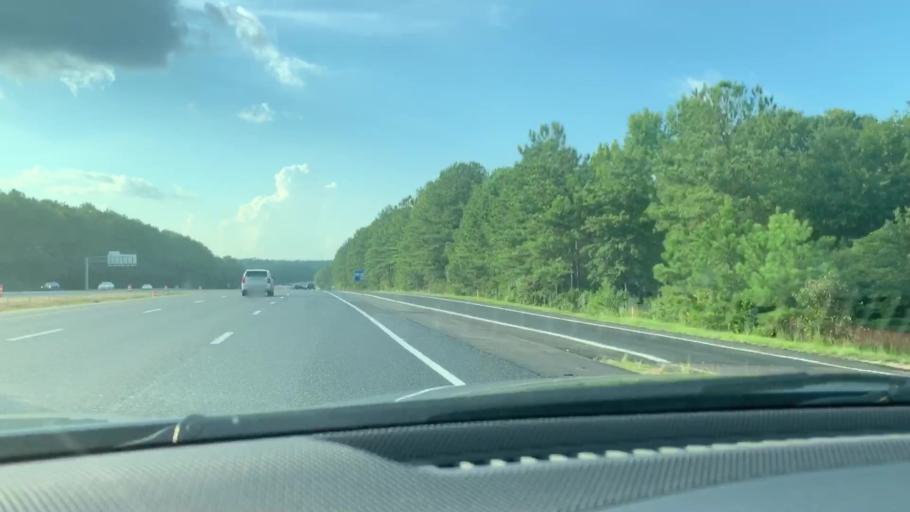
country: US
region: South Carolina
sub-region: Richland County
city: Dentsville
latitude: 34.0840
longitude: -80.9430
